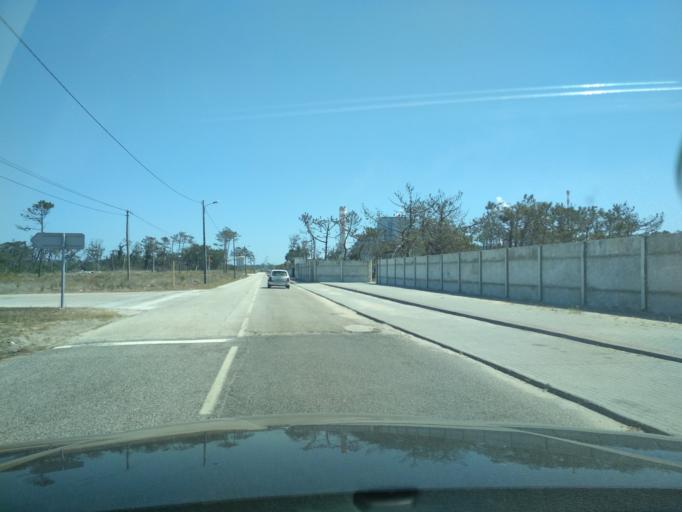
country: PT
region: Coimbra
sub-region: Figueira da Foz
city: Lavos
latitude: 40.0564
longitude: -8.8844
